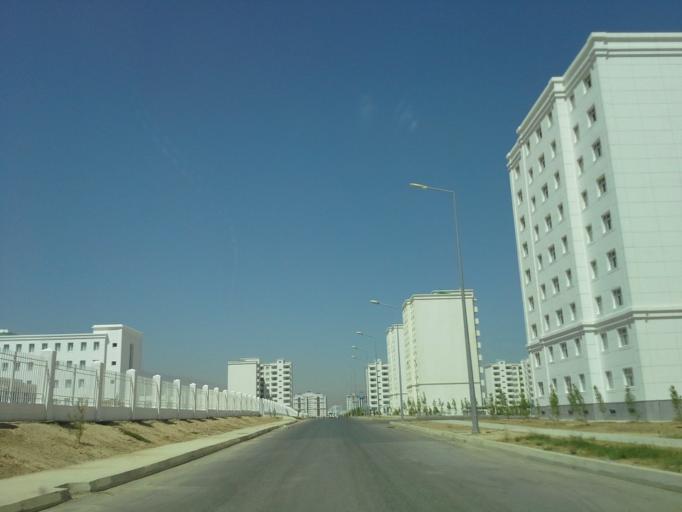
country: TM
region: Ahal
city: Ashgabat
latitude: 37.8884
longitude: 58.4110
